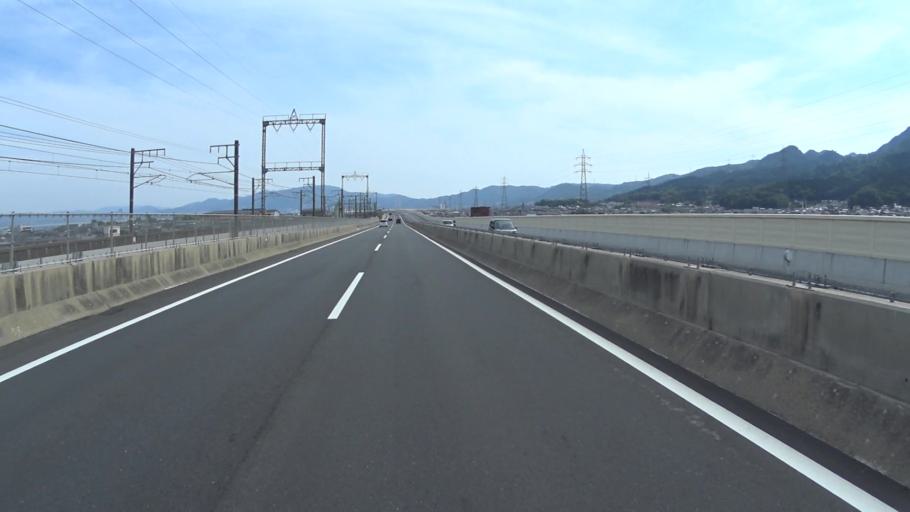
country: JP
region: Shiga Prefecture
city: Otsu-shi
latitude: 35.0683
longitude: 135.8771
